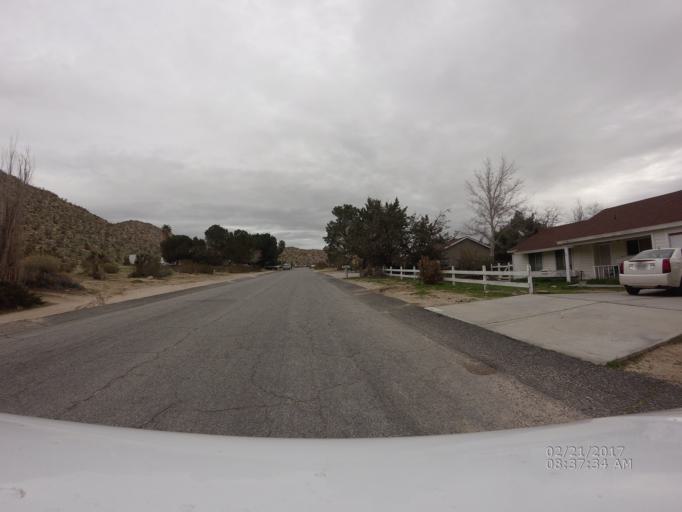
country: US
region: California
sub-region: Los Angeles County
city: Lake Los Angeles
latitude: 34.5990
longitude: -117.8344
